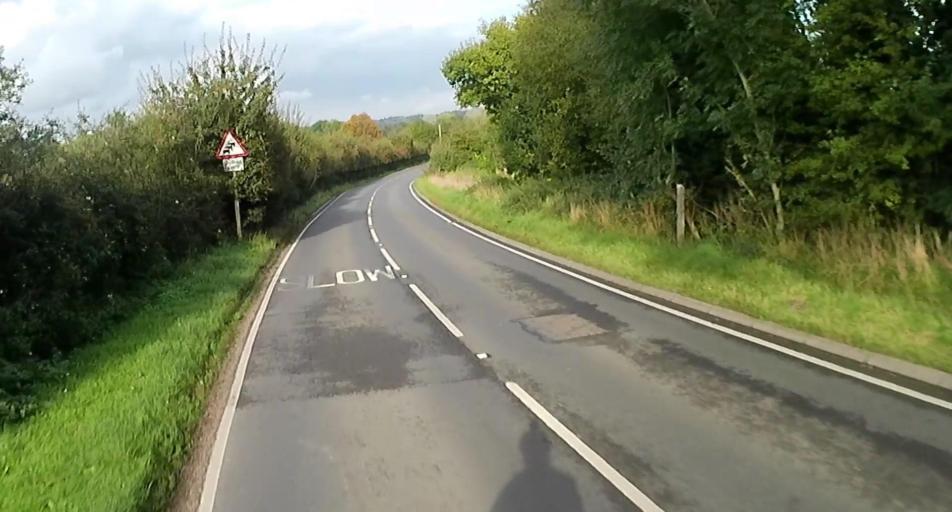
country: GB
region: England
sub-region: West Berkshire
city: Thatcham
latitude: 51.3866
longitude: -1.2485
